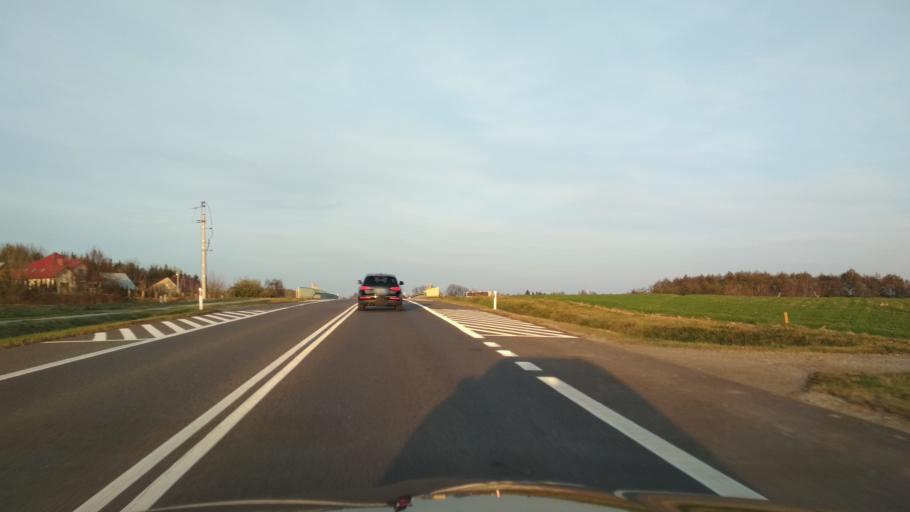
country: PL
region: Subcarpathian Voivodeship
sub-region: Powiat ropczycko-sedziszowski
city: Sedziszow Malopolski
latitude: 50.0662
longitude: 21.7347
